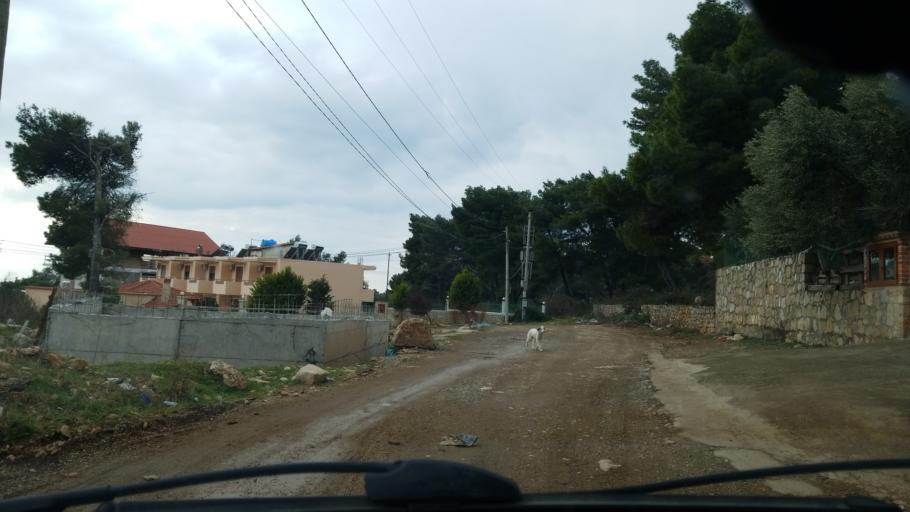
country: AL
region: Lezhe
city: Shengjin
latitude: 41.8139
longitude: 19.5827
